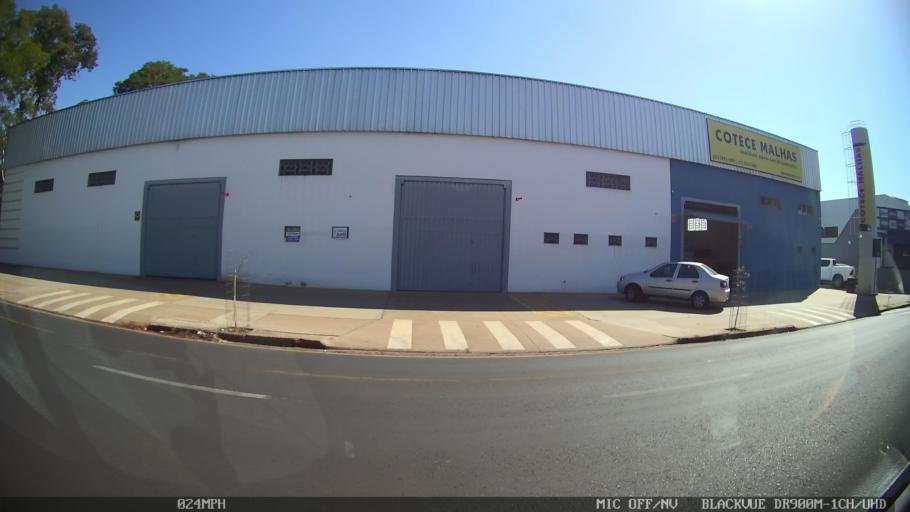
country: BR
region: Sao Paulo
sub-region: Sao Jose Do Rio Preto
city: Sao Jose do Rio Preto
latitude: -20.8080
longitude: -49.4043
